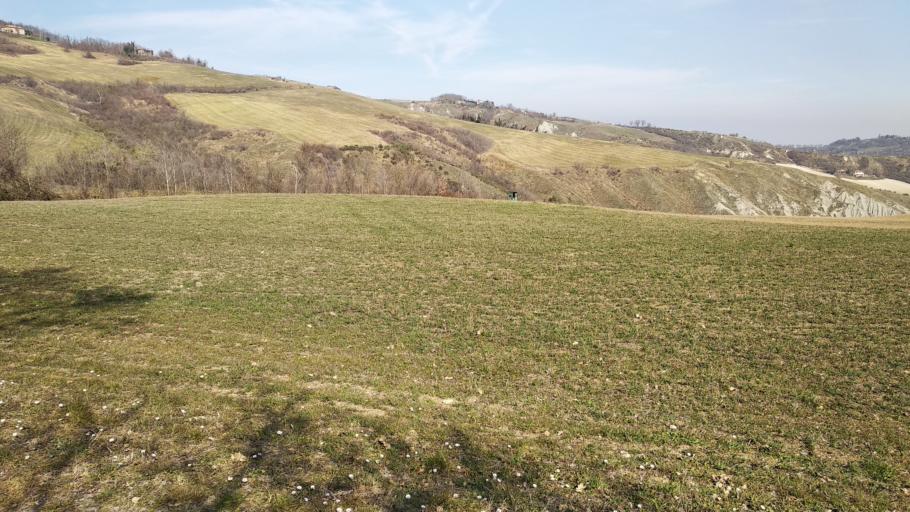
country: IT
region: Emilia-Romagna
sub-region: Provincia di Bologna
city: Osteria Grande
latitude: 44.3578
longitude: 11.5194
